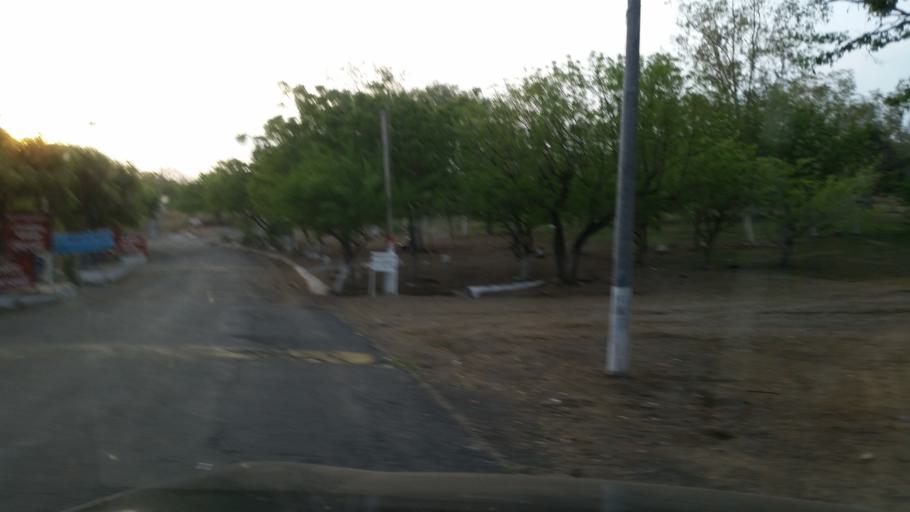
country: NI
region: Managua
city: Masachapa
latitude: 11.7729
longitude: -86.5075
